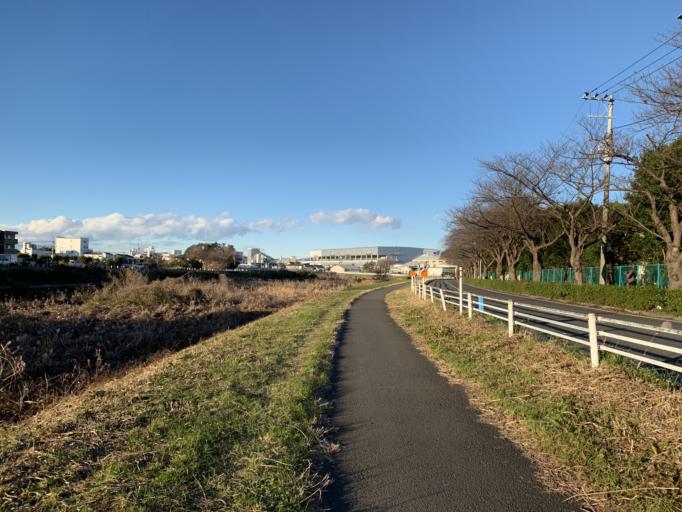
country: JP
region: Tokyo
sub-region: Machida-shi
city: Machida
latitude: 35.5153
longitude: 139.5514
